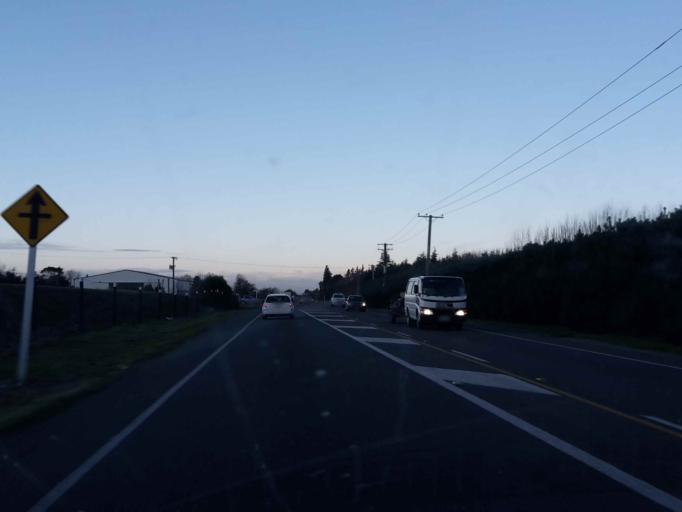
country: NZ
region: Canterbury
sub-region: Selwyn District
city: Prebbleton
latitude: -43.5619
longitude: 172.4567
